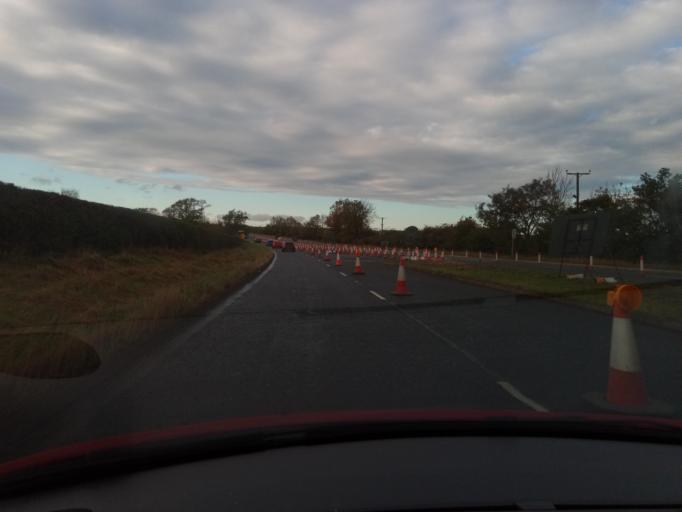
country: GB
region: England
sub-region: Darlington
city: Heighington
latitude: 54.5642
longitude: -1.5988
